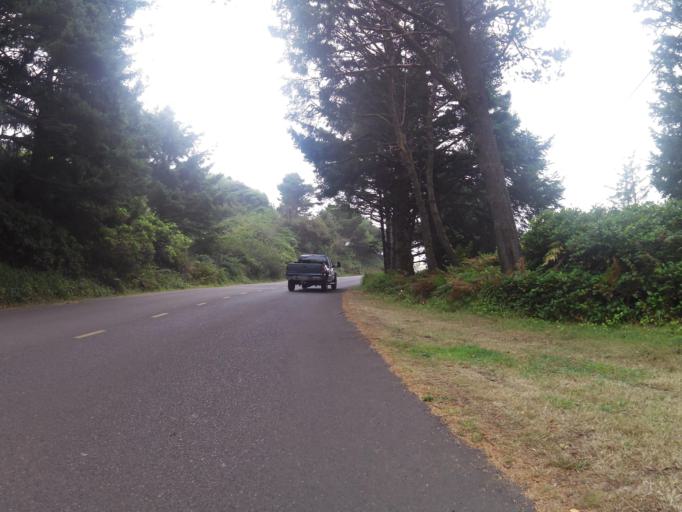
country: US
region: Oregon
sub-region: Lincoln County
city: Depoe Bay
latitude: 44.7269
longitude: -124.0566
